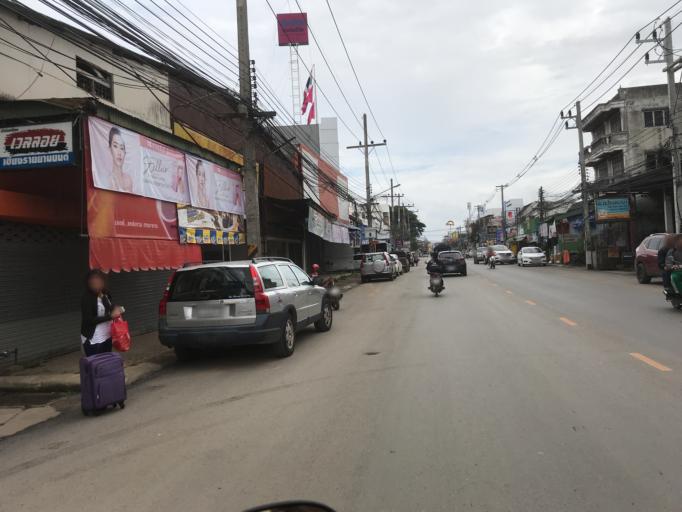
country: TH
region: Chiang Rai
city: Chiang Rai
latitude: 19.8953
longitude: 99.8316
